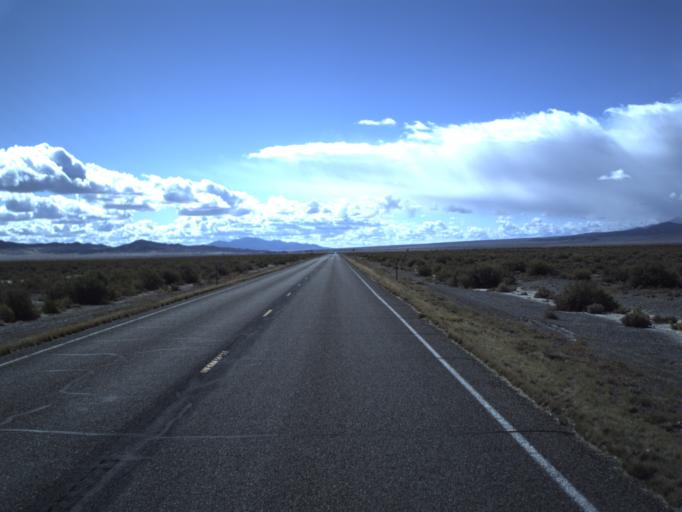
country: US
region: Nevada
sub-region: White Pine County
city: McGill
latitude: 39.0489
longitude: -114.0364
